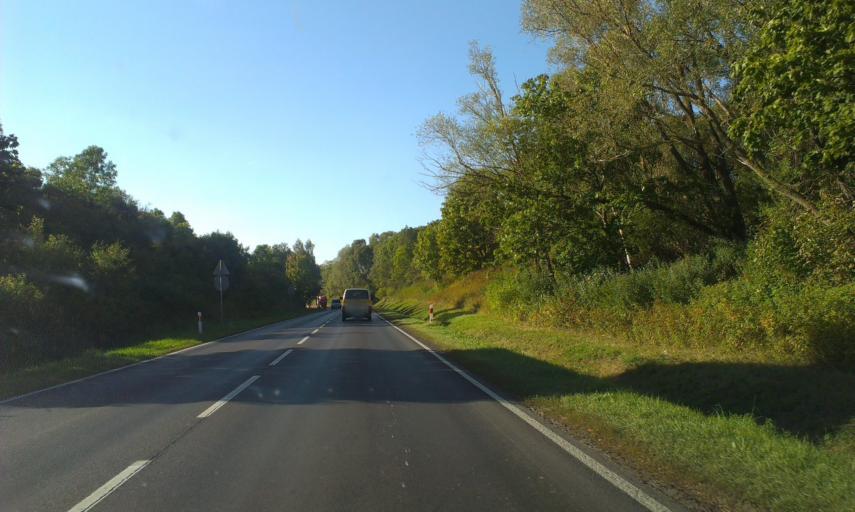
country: PL
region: Kujawsko-Pomorskie
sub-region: Powiat swiecki
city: Swiecie
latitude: 53.4111
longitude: 18.3743
